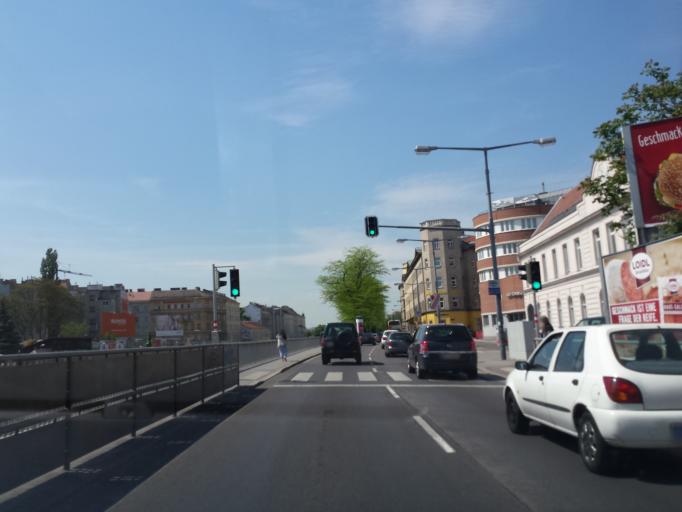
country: AT
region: Vienna
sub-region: Wien Stadt
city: Vienna
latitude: 48.1841
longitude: 16.3268
